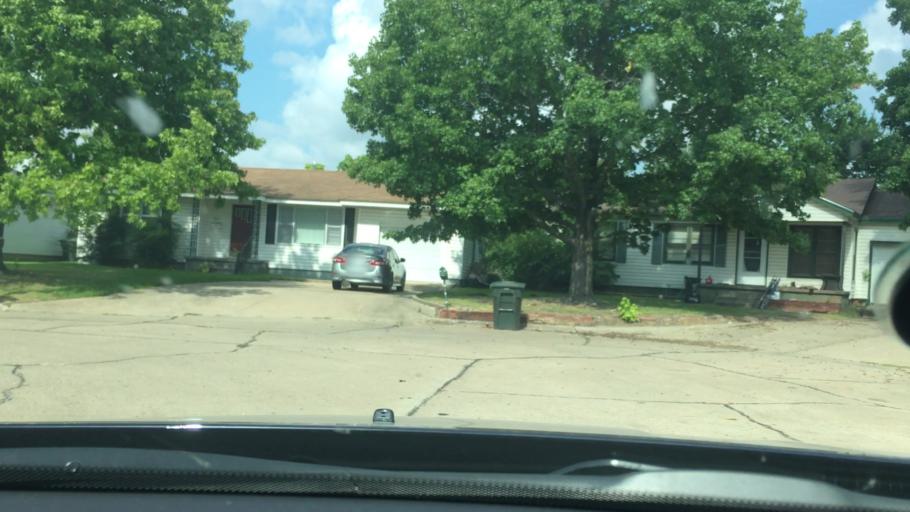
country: US
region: Oklahoma
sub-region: Bryan County
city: Durant
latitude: 34.0044
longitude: -96.3919
